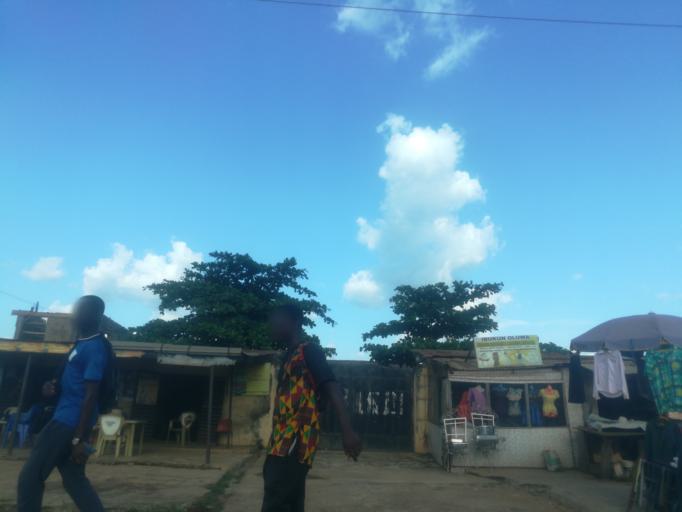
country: NG
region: Oyo
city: Egbeda
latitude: 7.4322
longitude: 3.9836
